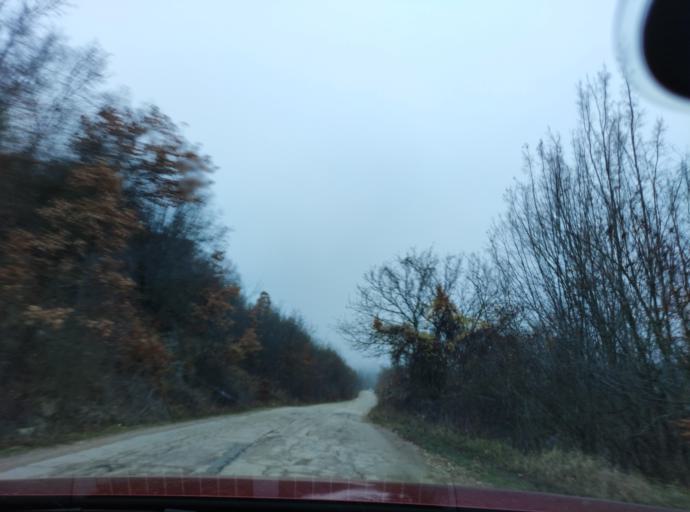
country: BG
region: Lovech
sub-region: Obshtina Yablanitsa
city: Yablanitsa
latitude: 43.1131
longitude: 24.0668
